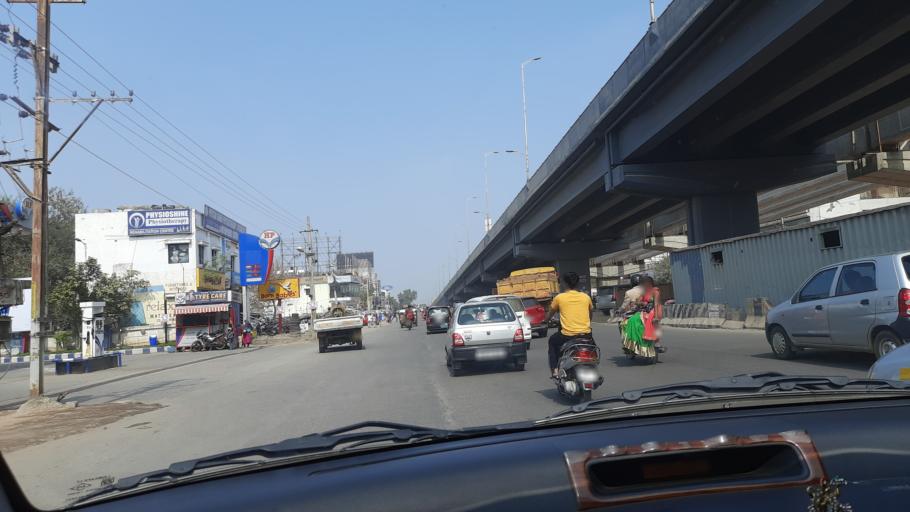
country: IN
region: Telangana
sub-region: Rangareddi
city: Lal Bahadur Nagar
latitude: 17.3537
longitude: 78.5557
